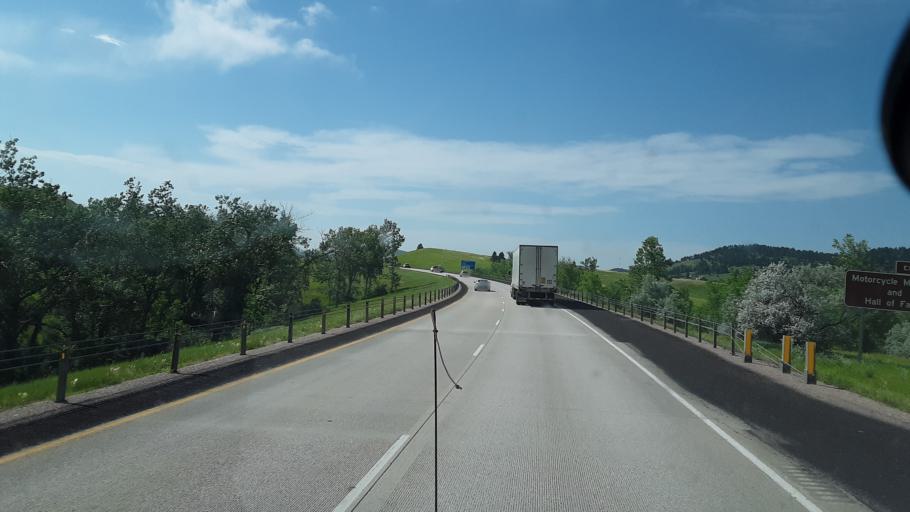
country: US
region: South Dakota
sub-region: Meade County
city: Sturgis
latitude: 44.3868
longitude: -103.4867
